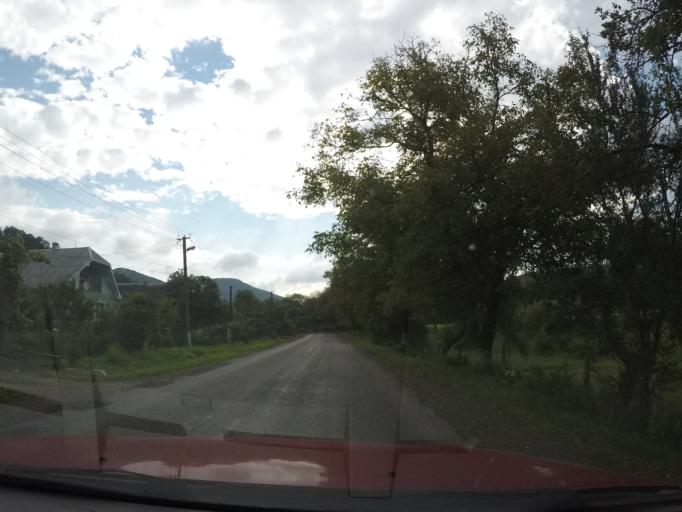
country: UA
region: Zakarpattia
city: Velykyi Bereznyi
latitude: 48.9512
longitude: 22.5398
